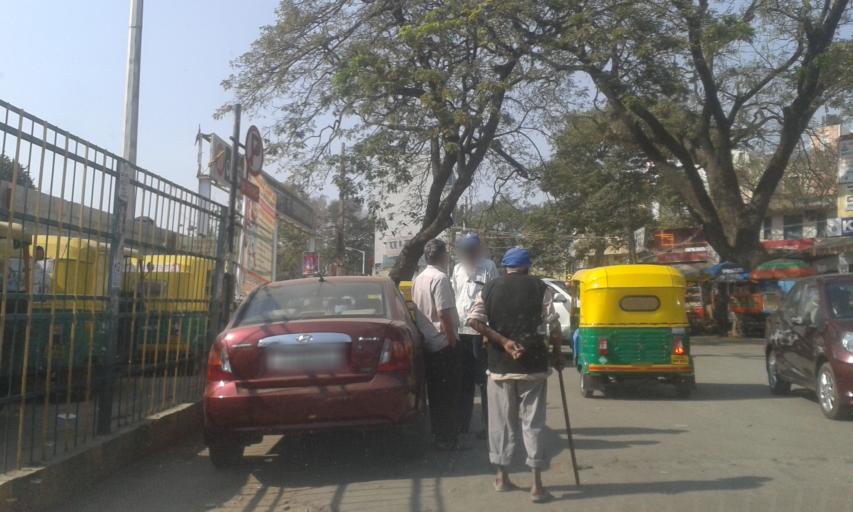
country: IN
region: Karnataka
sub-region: Bangalore Urban
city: Bangalore
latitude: 13.0219
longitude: 77.5531
